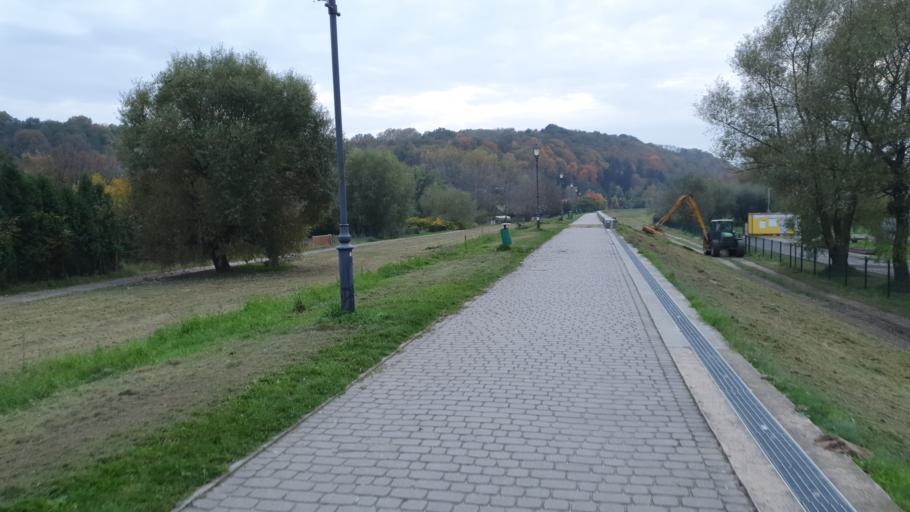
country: PL
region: Lublin Voivodeship
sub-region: Powiat pulawski
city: Kazimierz Dolny
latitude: 51.3234
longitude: 21.9431
